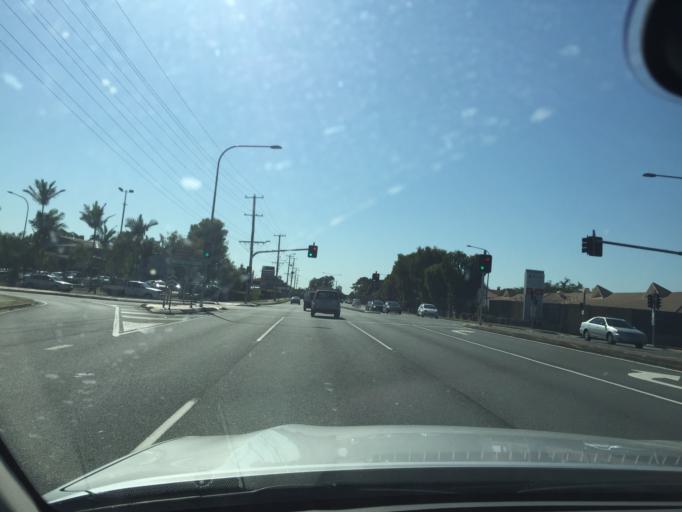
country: AU
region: Queensland
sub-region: Gold Coast
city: Clear Island Waters
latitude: -28.0318
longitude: 153.3914
